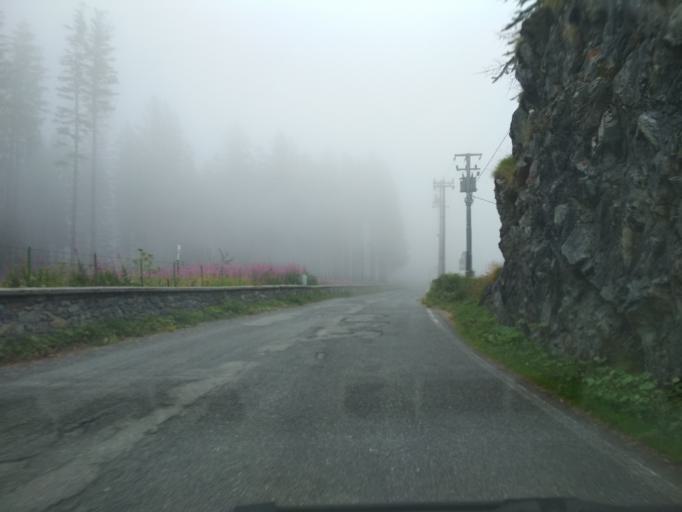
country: IT
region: Piedmont
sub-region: Provincia di Torino
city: Balme
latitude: 45.3034
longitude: 7.1848
